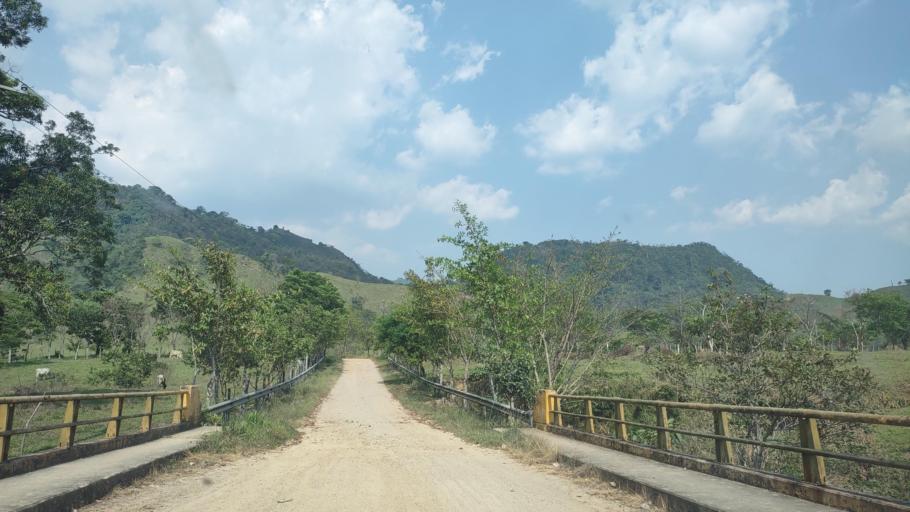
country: MX
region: Chiapas
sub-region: Tecpatan
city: Raudales Malpaso
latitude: 17.3460
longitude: -93.7568
